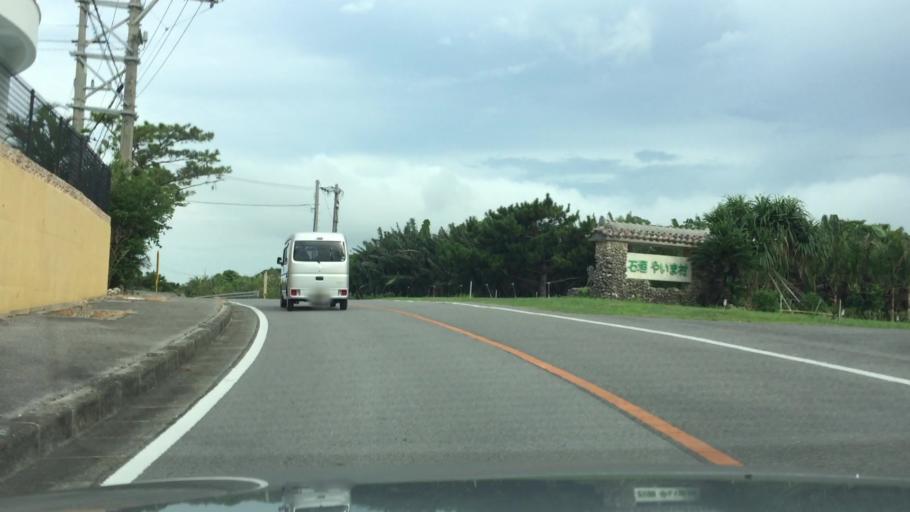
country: JP
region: Okinawa
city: Ishigaki
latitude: 24.4057
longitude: 124.1452
